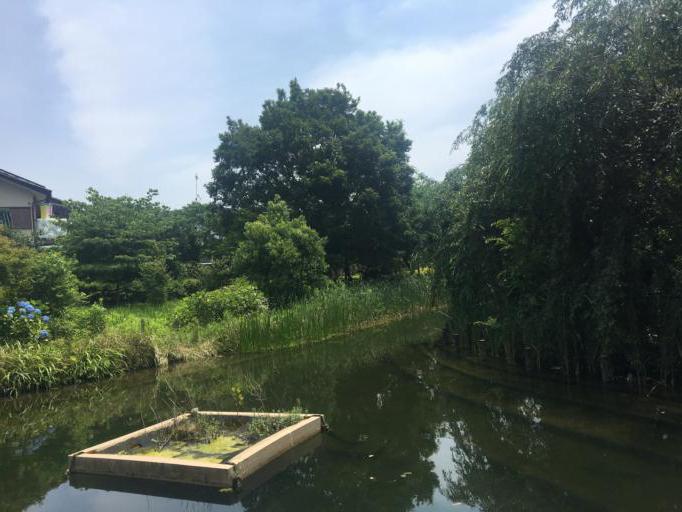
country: JP
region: Tokyo
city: Tanashicho
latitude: 35.7413
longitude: 139.5396
